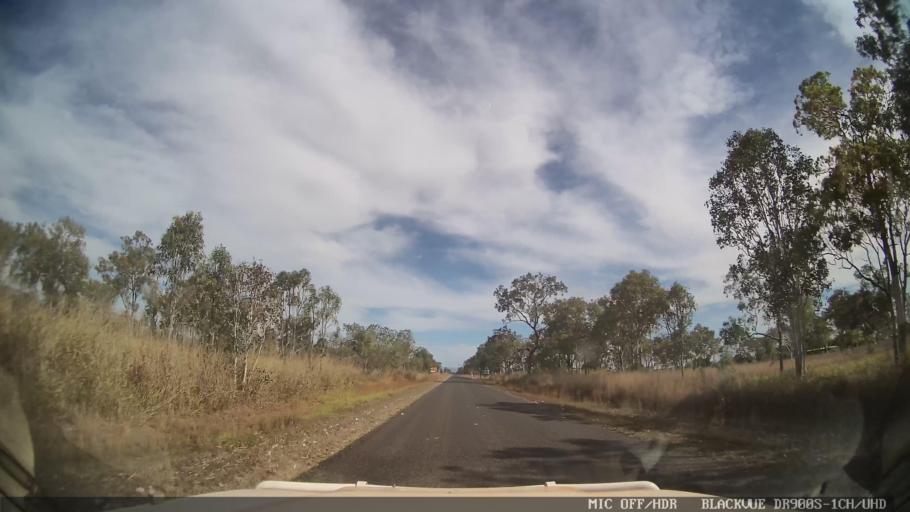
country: AU
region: Queensland
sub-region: Tablelands
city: Mareeba
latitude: -16.9421
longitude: 145.4164
